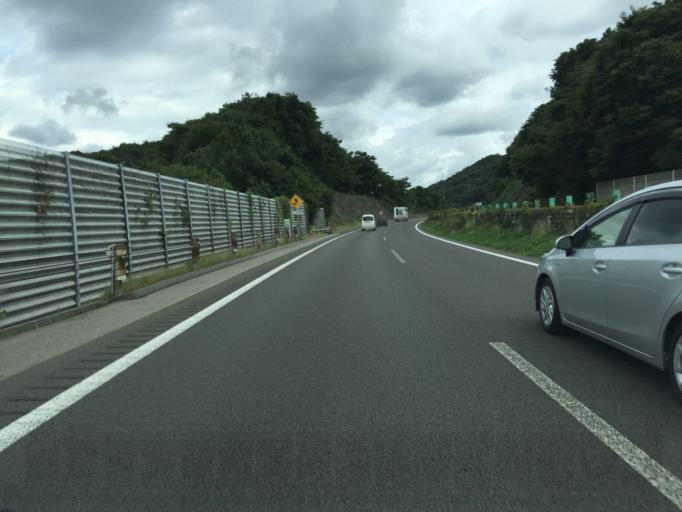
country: JP
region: Miyagi
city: Shiroishi
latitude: 37.9360
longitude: 140.6091
